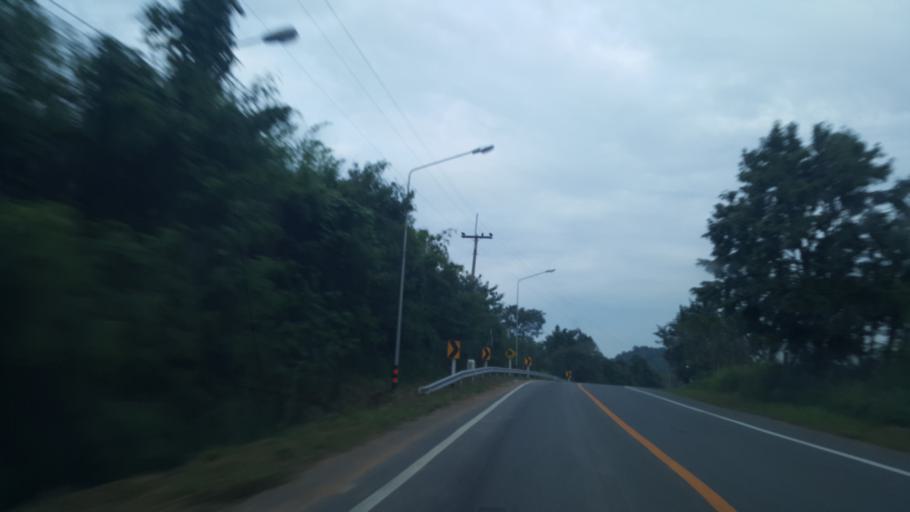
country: TH
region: Chon Buri
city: Ban Talat Bueng
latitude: 12.9680
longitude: 101.0100
